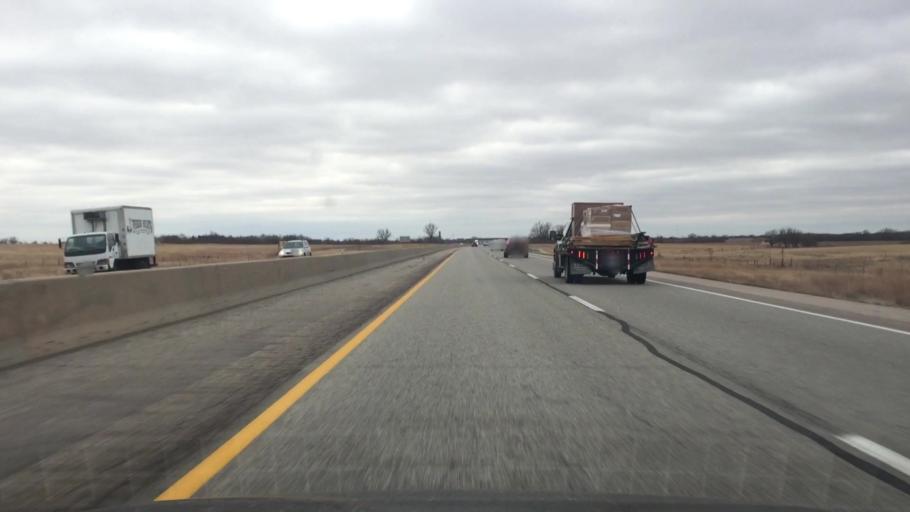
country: US
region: Kansas
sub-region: Butler County
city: El Dorado
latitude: 38.0362
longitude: -96.6520
